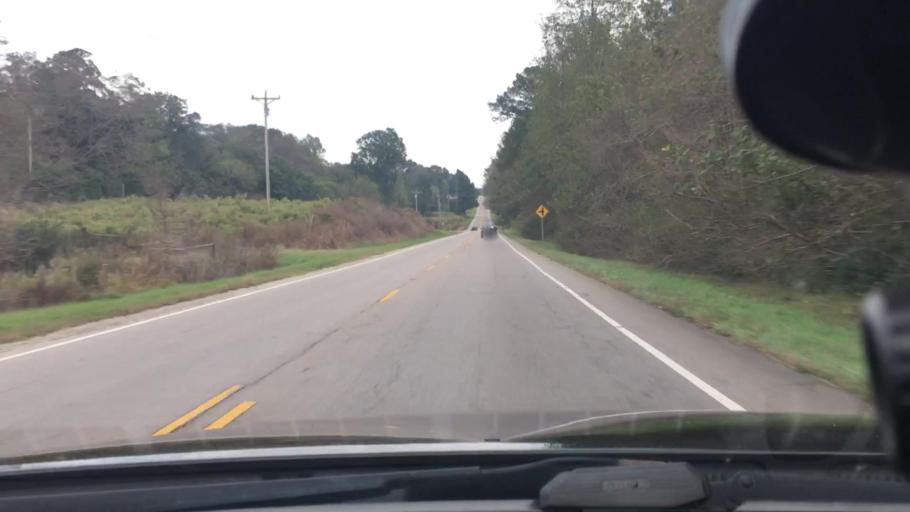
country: US
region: North Carolina
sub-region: Moore County
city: Robbins
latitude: 35.3907
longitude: -79.5144
